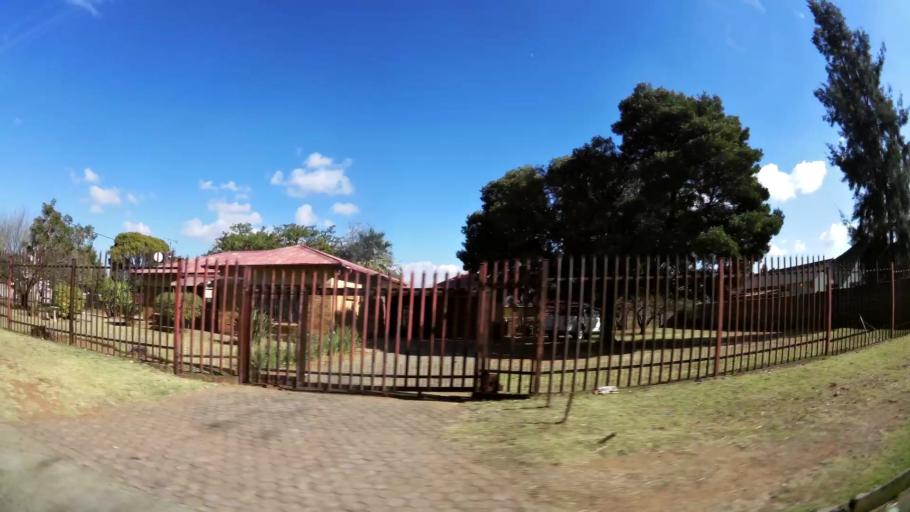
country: ZA
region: Gauteng
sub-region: City of Johannesburg Metropolitan Municipality
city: Roodepoort
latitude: -26.1353
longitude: 27.8372
